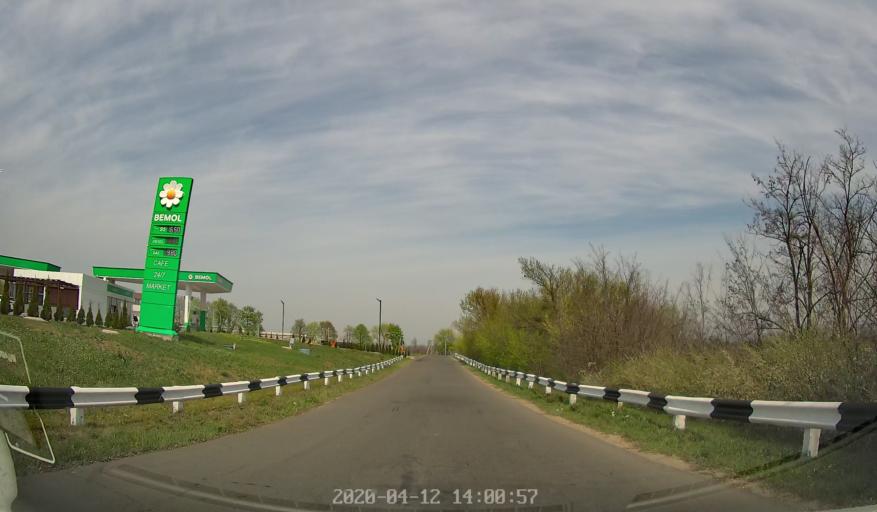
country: MD
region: Chisinau
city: Stauceni
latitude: 47.1132
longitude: 28.8634
